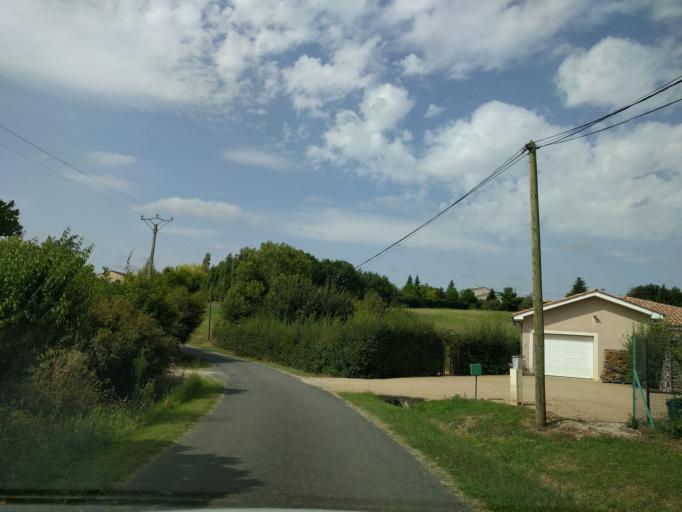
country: FR
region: Midi-Pyrenees
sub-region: Departement du Tarn
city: Saix
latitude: 43.6503
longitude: 2.2001
